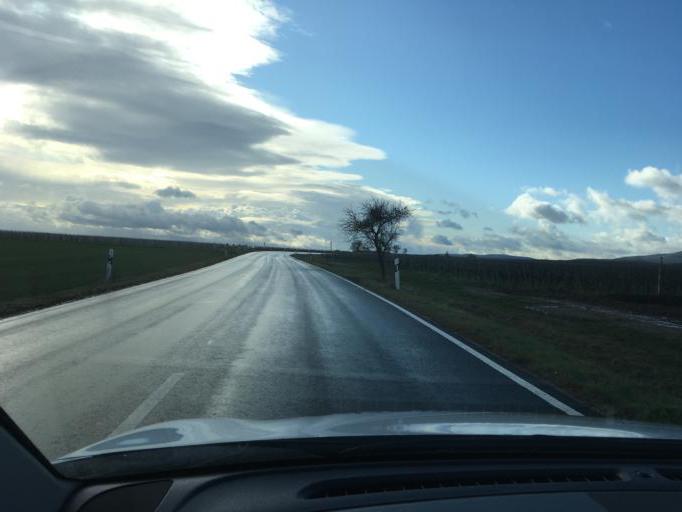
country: DE
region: Rheinland-Pfalz
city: Kirchheim an der Weinstrasse
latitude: 49.5333
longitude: 8.1805
